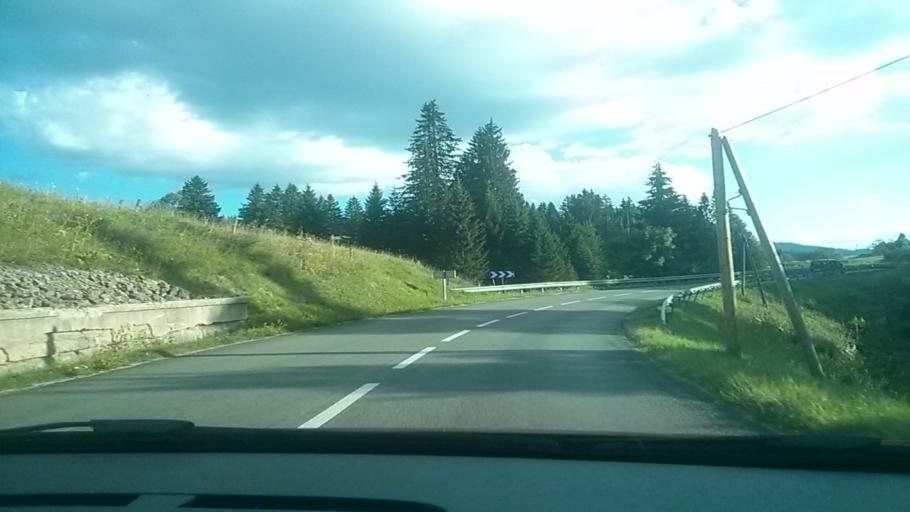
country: FR
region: Franche-Comte
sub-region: Departement du Jura
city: Les Rousses
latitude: 46.4819
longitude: 6.0888
